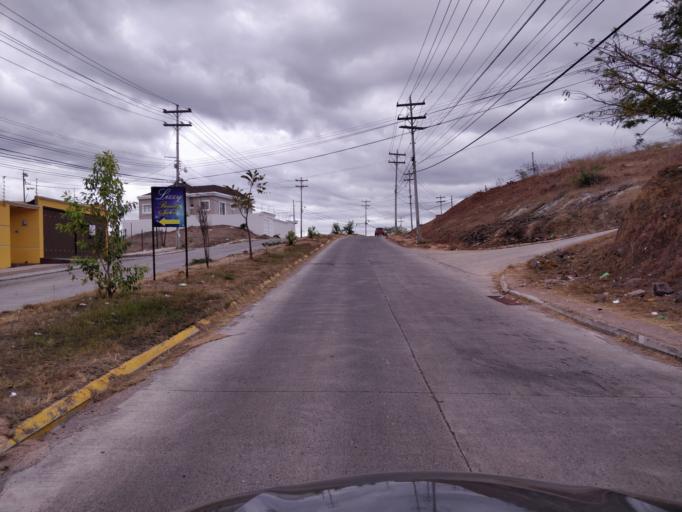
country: HN
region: Francisco Morazan
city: Yaguacire
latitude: 14.0388
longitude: -87.2372
